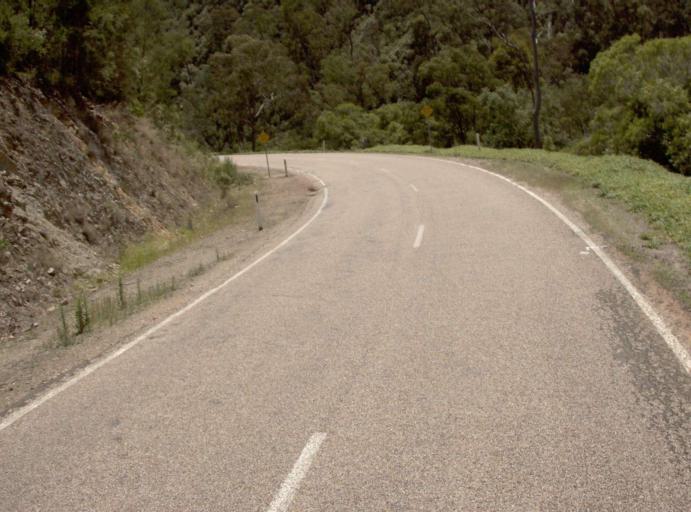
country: AU
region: Victoria
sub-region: East Gippsland
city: Lakes Entrance
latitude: -37.5305
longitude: 147.8534
